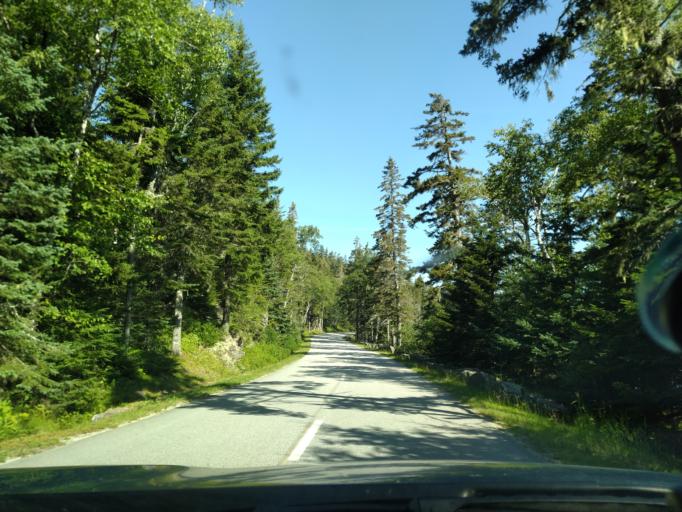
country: US
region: Maine
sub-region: Hancock County
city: Gouldsboro
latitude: 44.3447
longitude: -68.0450
